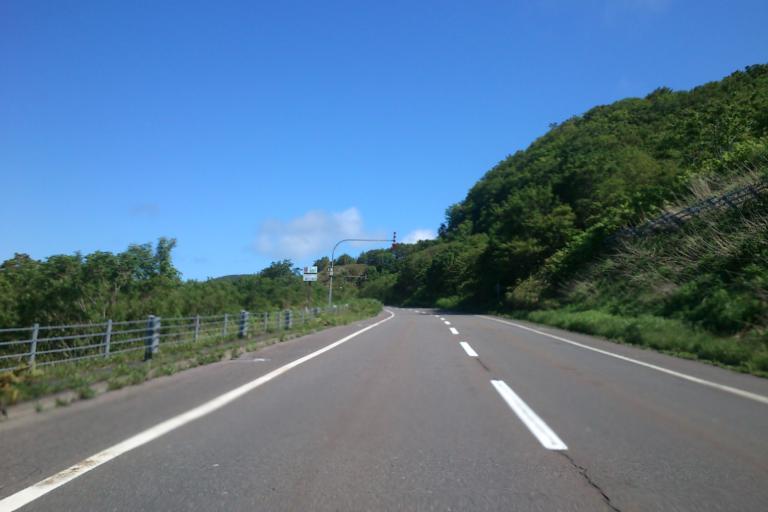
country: JP
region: Hokkaido
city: Ishikari
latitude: 43.4952
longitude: 141.3739
